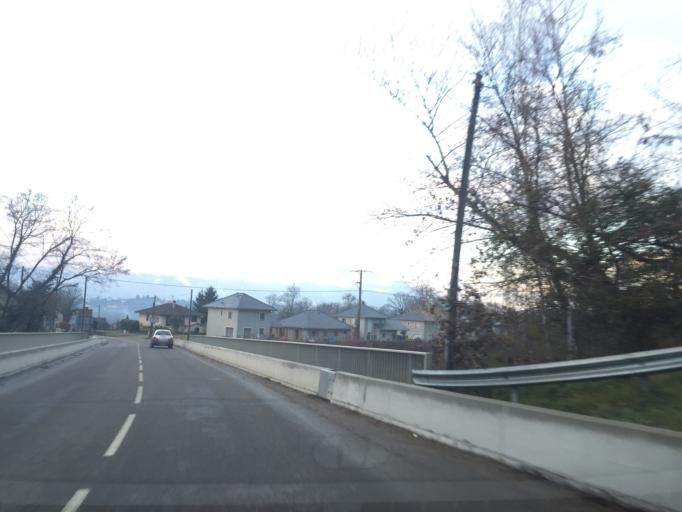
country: FR
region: Rhone-Alpes
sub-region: Departement de la Savoie
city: Drumettaz-Clarafond
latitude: 45.6588
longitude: 5.9272
